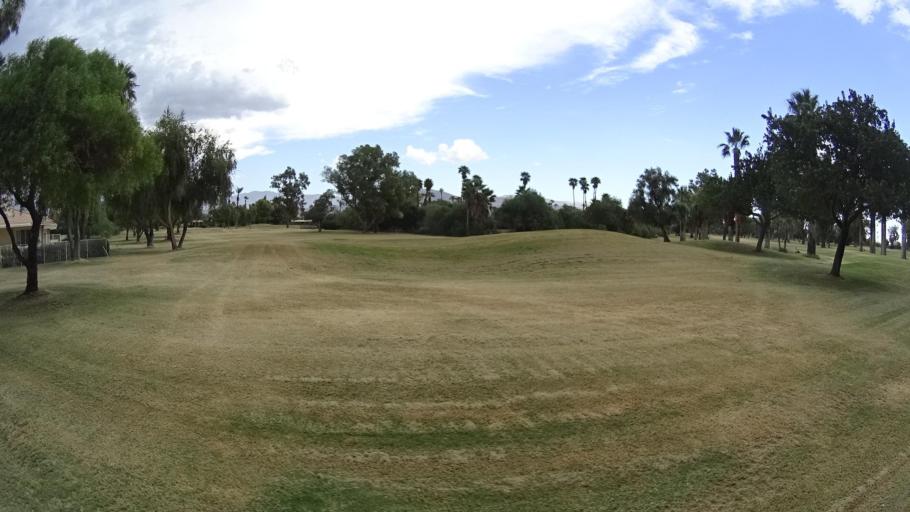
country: US
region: California
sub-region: San Diego County
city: Borrego Springs
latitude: 33.2858
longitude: -116.3950
